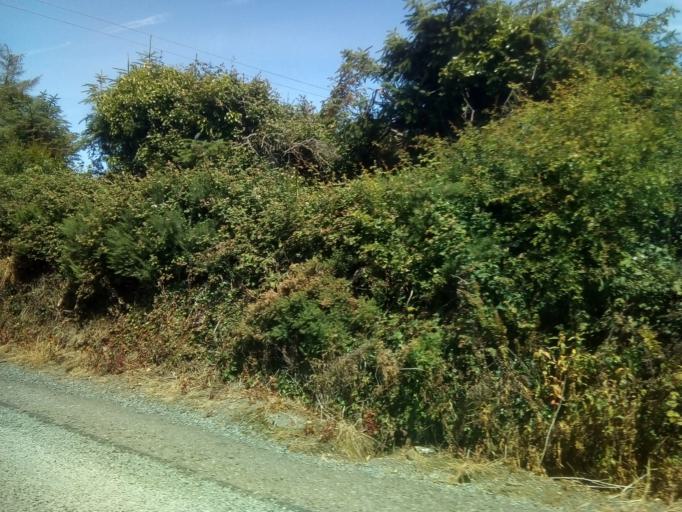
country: IE
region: Leinster
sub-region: Loch Garman
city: Loch Garman
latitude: 52.2468
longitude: -6.6080
